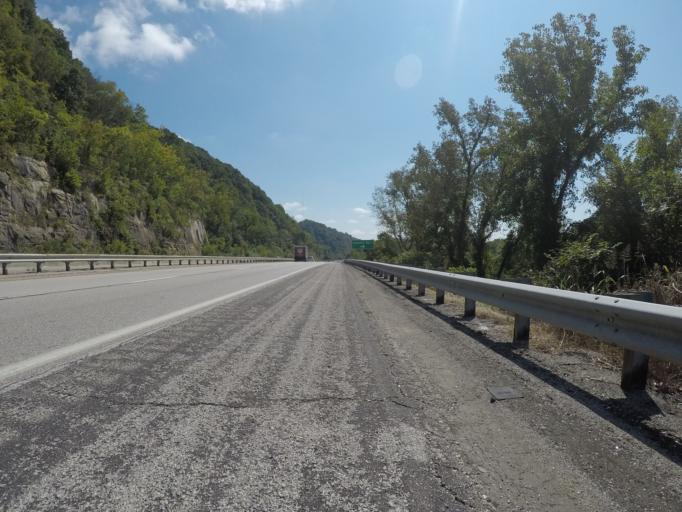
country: US
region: Kentucky
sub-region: Boyd County
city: Ashland
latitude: 38.4731
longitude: -82.6092
